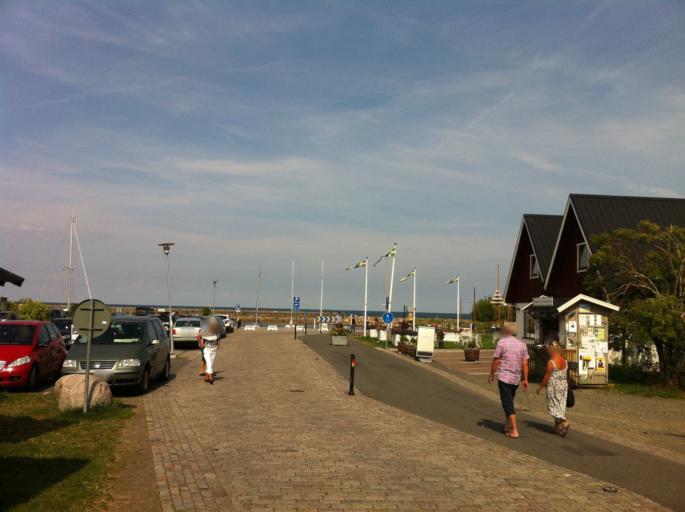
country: SE
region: Skane
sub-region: Simrishamns Kommun
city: Kivik
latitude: 55.6870
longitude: 14.2275
